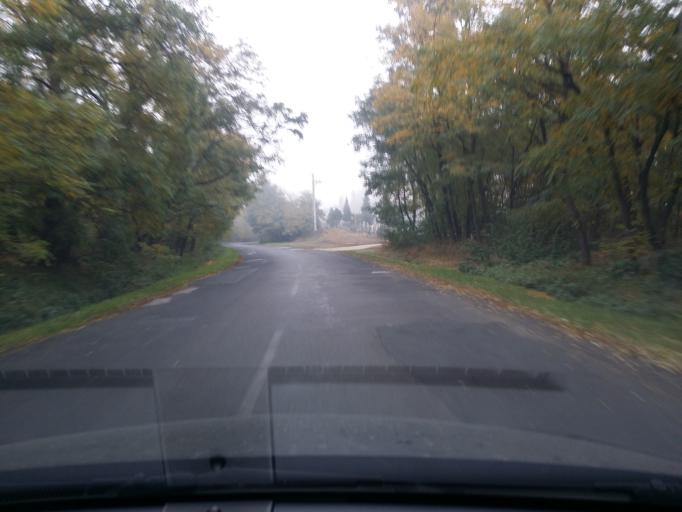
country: HU
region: Szabolcs-Szatmar-Bereg
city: Nyirbogdany
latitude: 48.0671
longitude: 21.8607
